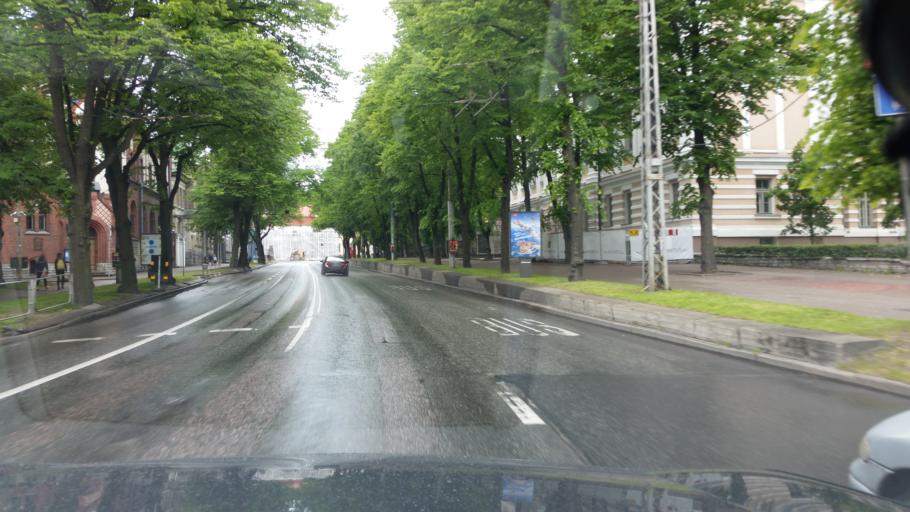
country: EE
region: Harju
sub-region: Tallinna linn
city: Tallinn
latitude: 59.4340
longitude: 24.7502
